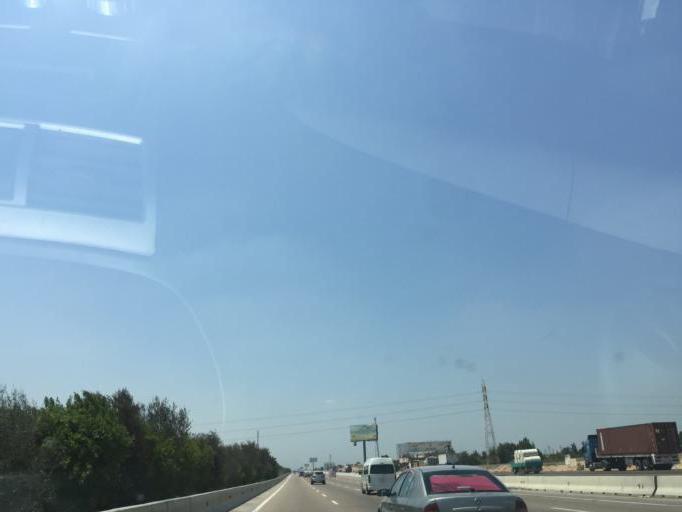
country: EG
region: Al Buhayrah
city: Beheira
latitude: 30.4157
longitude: 30.3539
